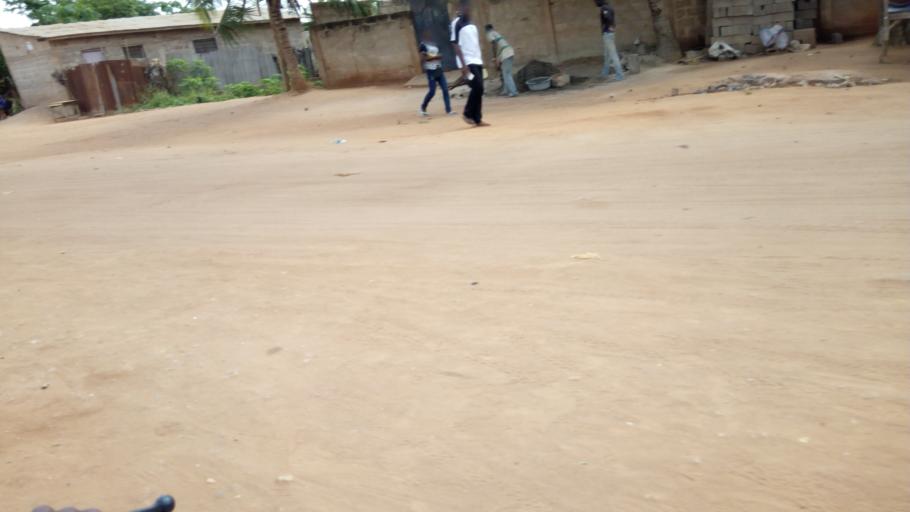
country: TG
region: Maritime
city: Lome
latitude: 6.2217
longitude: 1.1601
